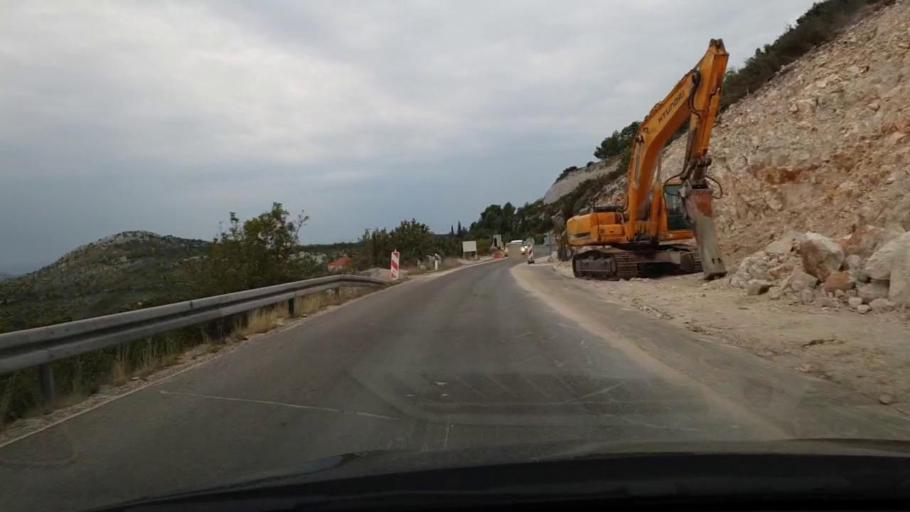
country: HR
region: Dubrovacko-Neretvanska
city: Cibaca
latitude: 42.6500
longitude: 18.1594
